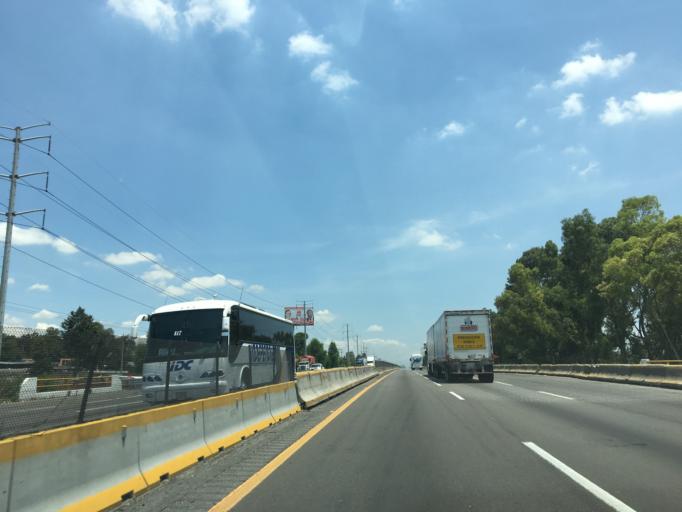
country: MX
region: Puebla
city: Ocotlan
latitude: 19.1439
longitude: -98.2805
